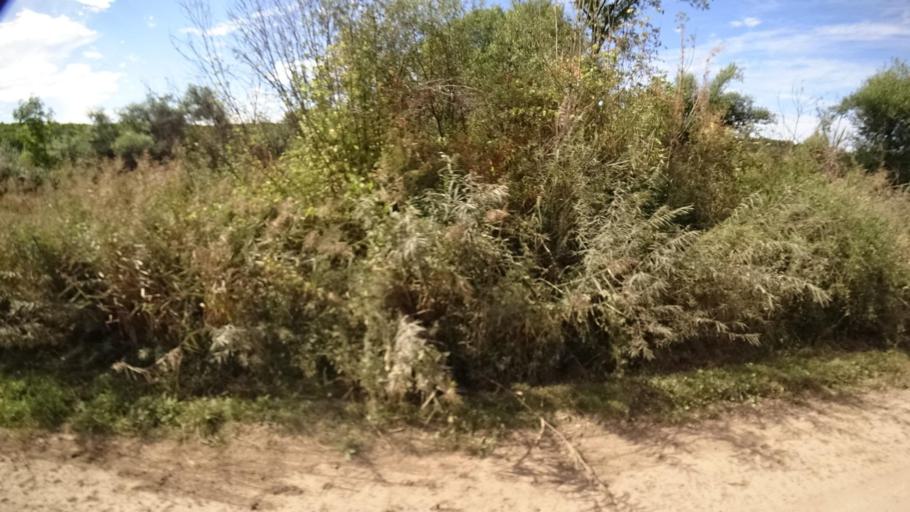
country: RU
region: Primorskiy
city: Yakovlevka
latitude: 44.3884
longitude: 133.5407
